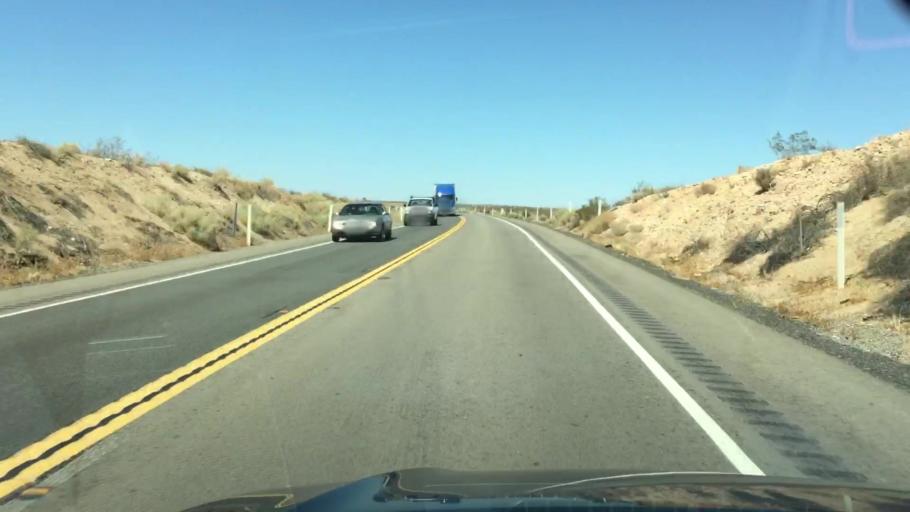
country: US
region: California
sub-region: Kern County
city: Boron
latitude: 35.0674
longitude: -117.5593
